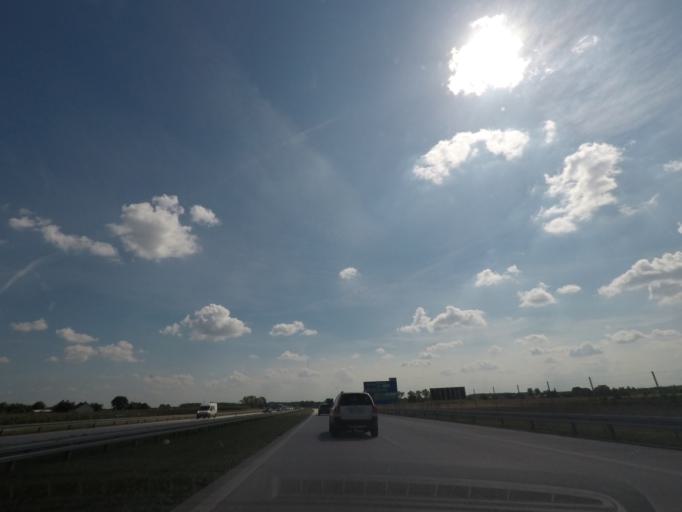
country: PL
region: Lodz Voivodeship
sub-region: Powiat lodzki wschodni
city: Andrespol
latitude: 51.7654
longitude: 19.5969
